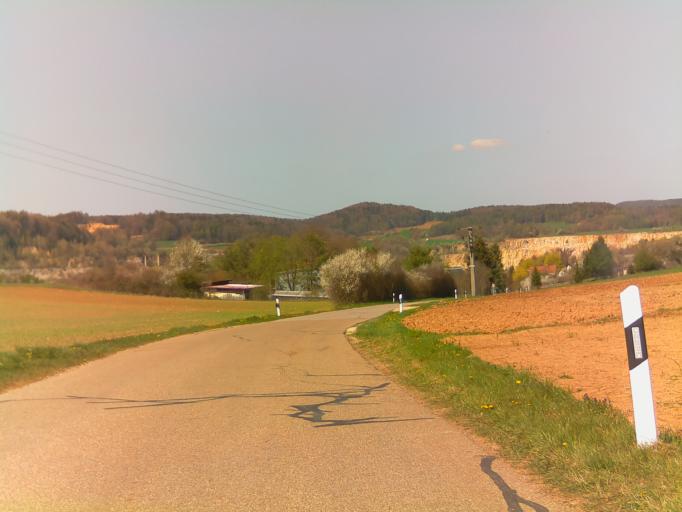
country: DE
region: Bavaria
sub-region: Upper Palatinate
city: Weigendorf
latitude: 49.4893
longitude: 11.5618
